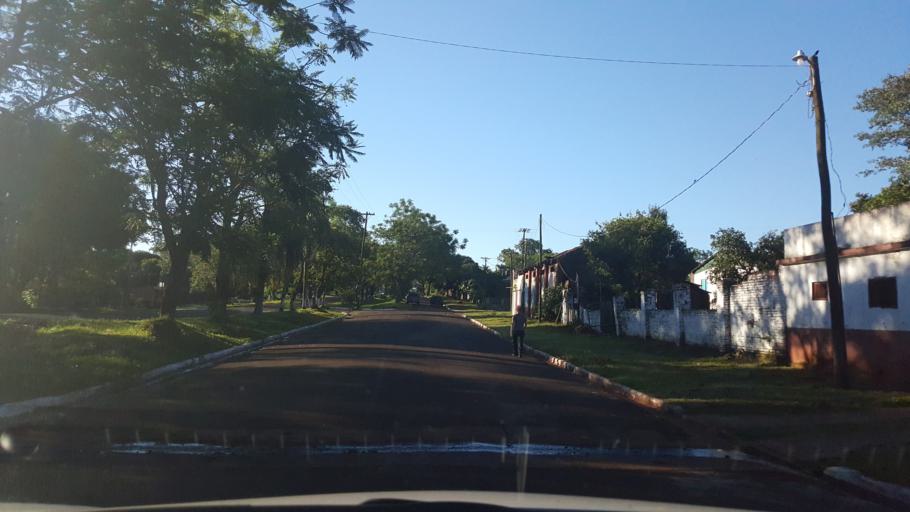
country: AR
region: Misiones
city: Gobernador Roca
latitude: -27.1315
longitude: -55.5084
